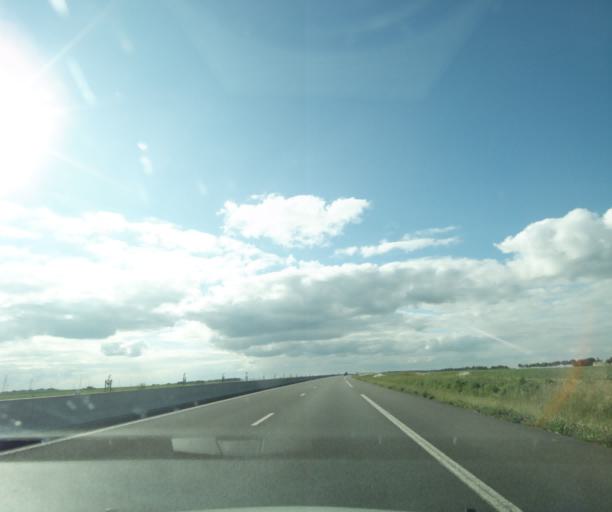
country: FR
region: Centre
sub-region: Departement d'Eure-et-Loir
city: Sours
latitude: 48.3651
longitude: 1.5976
